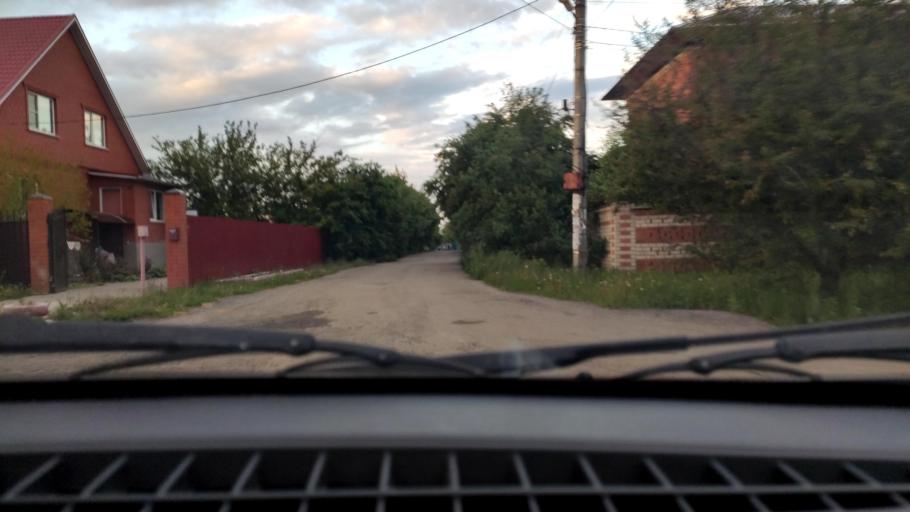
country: RU
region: Voronezj
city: Somovo
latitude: 51.6799
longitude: 39.3234
